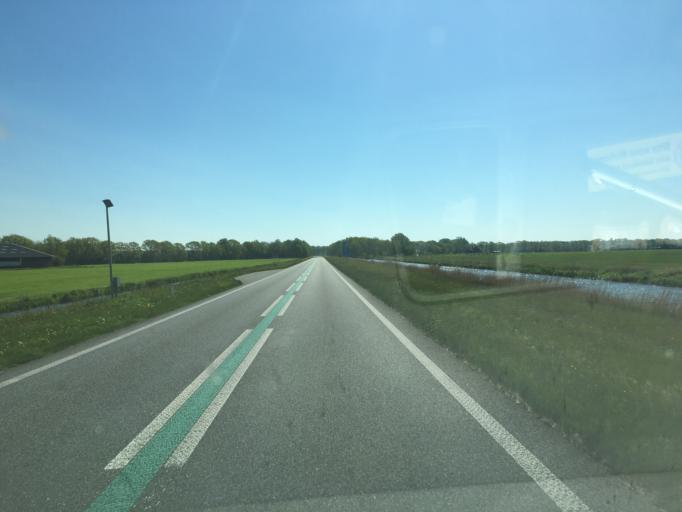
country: NL
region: Friesland
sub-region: Gemeente Gaasterlan-Sleat
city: Oudemirdum
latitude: 52.8789
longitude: 5.5042
